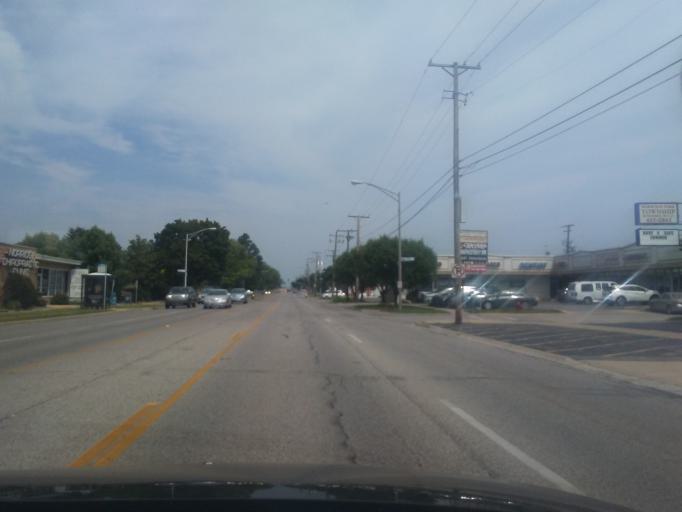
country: US
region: Illinois
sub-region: Cook County
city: Norridge
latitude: 41.9668
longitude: -87.8236
